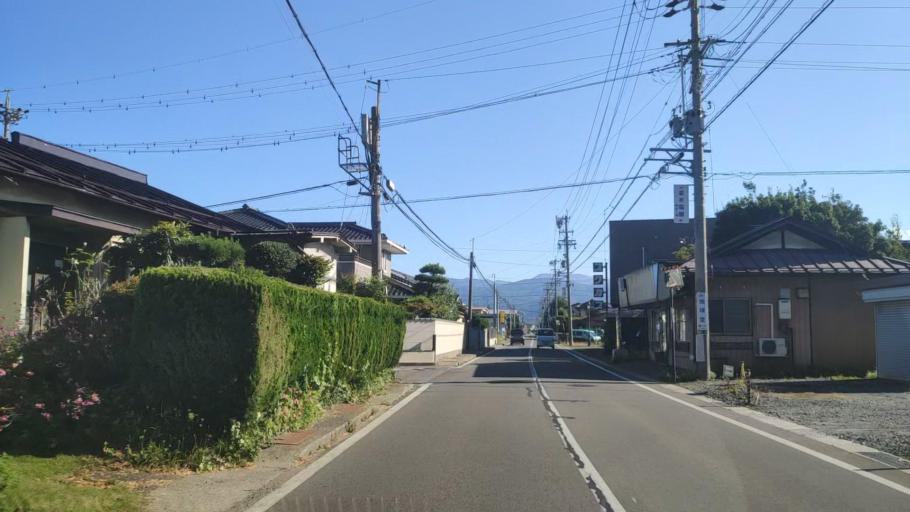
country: JP
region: Nagano
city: Okaya
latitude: 36.0556
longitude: 138.0567
